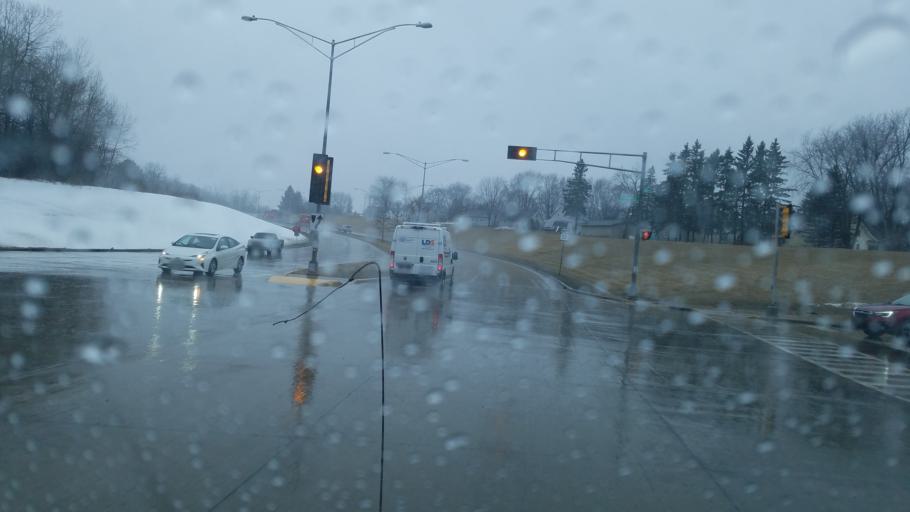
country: US
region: Wisconsin
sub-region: Wood County
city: Marshfield
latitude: 44.6706
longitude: -90.1817
